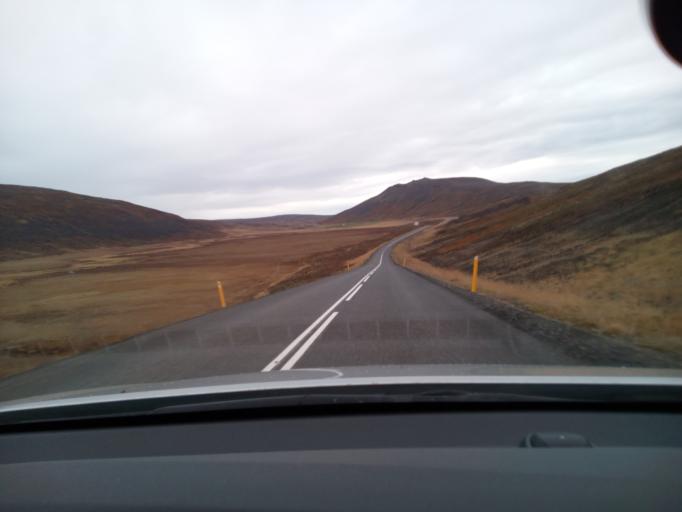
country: IS
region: Northeast
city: Laugar
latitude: 65.8190
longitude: -17.2744
